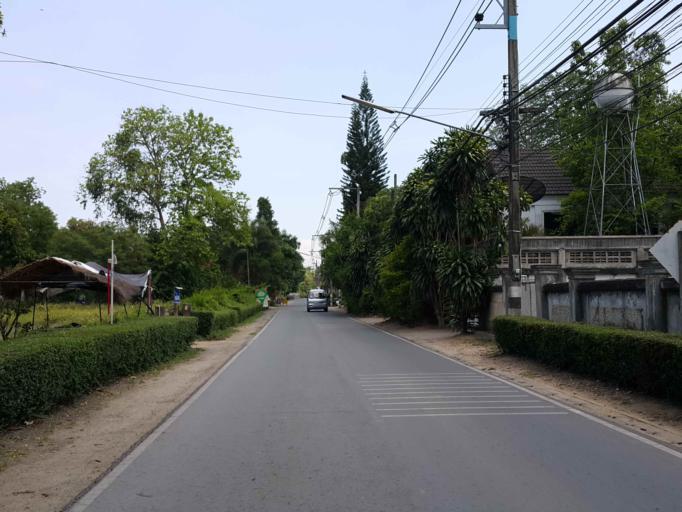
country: TH
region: Chiang Mai
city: Chiang Mai
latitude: 18.8372
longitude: 98.9911
